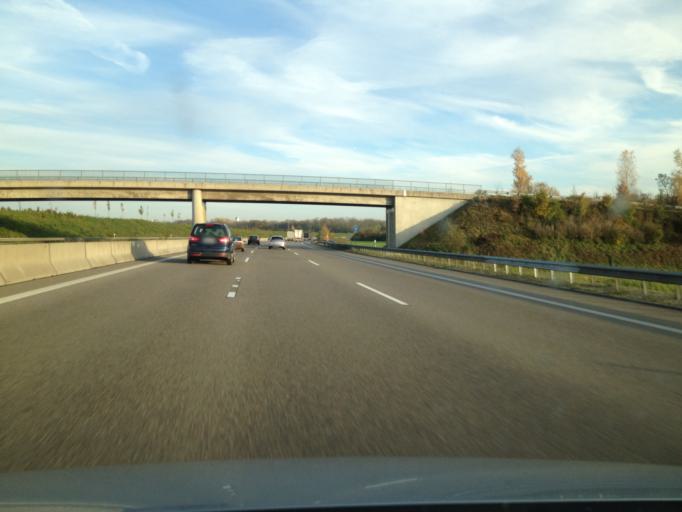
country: DE
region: Bavaria
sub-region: Swabia
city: Leipheim
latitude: 48.4571
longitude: 10.1900
